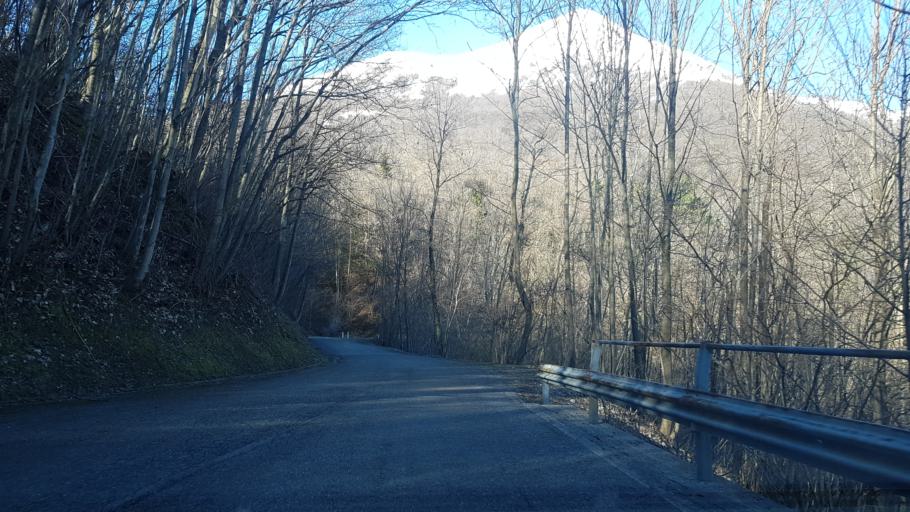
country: IT
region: Friuli Venezia Giulia
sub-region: Provincia di Udine
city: Isola
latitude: 46.2635
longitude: 13.2023
